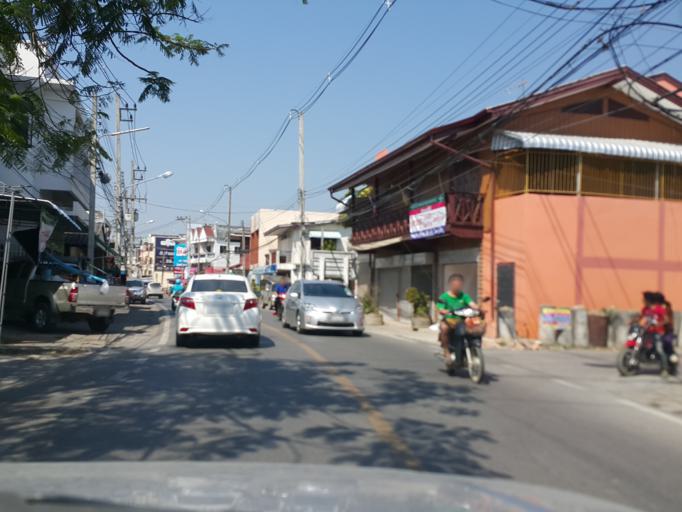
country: TH
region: Chiang Mai
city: San Kamphaeng
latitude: 18.7412
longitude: 99.1240
